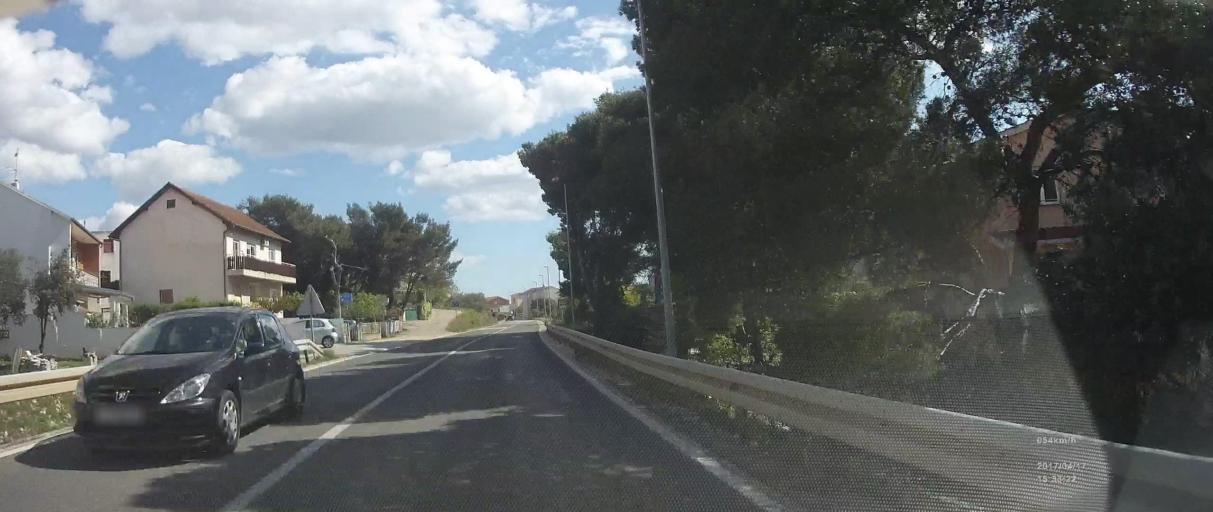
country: HR
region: Sibensko-Kniniska
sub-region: Grad Sibenik
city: Brodarica
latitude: 43.6868
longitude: 15.9113
